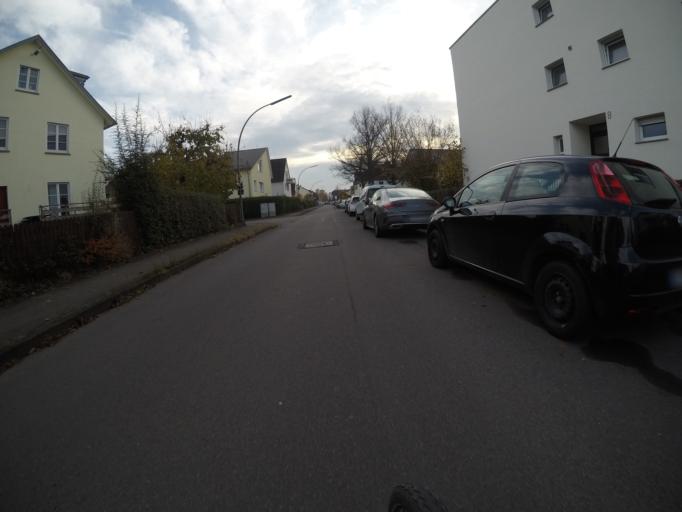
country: DE
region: Baden-Wuerttemberg
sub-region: Regierungsbezirk Stuttgart
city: Leinfelden-Echterdingen
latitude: 48.6868
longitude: 9.1612
